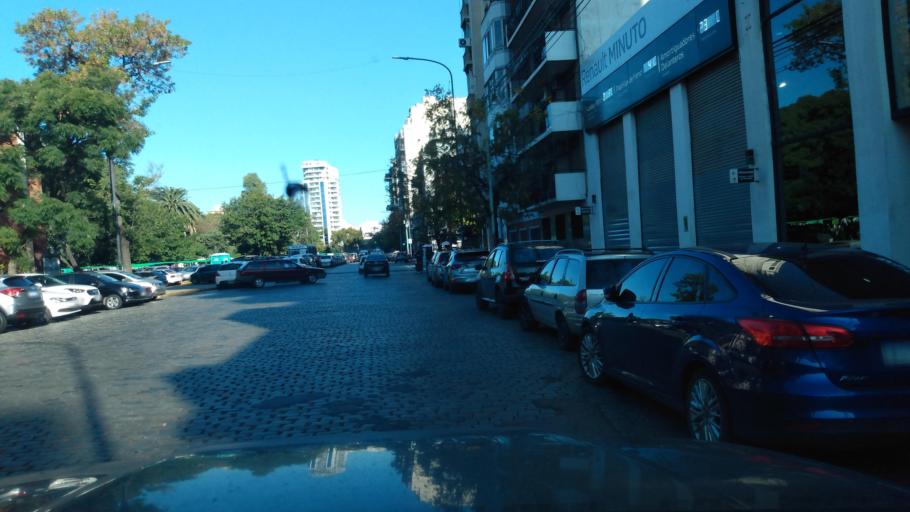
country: AR
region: Buenos Aires F.D.
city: Colegiales
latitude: -34.6059
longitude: -58.4391
